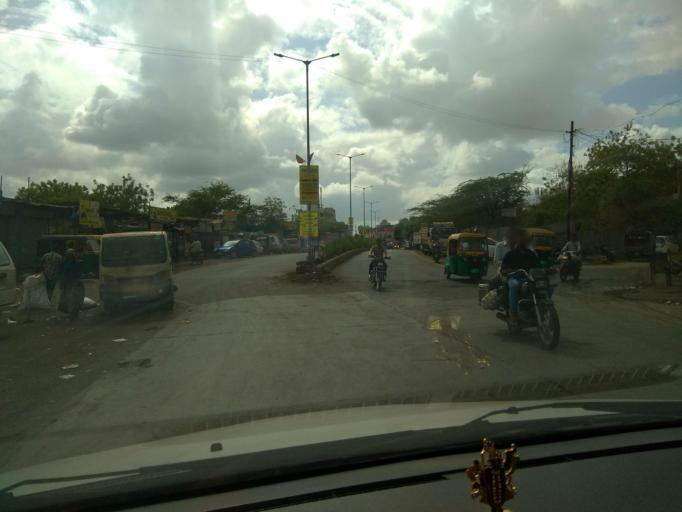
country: IN
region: Gujarat
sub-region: Bhavnagar
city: Bhavnagar
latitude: 21.7739
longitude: 72.1471
